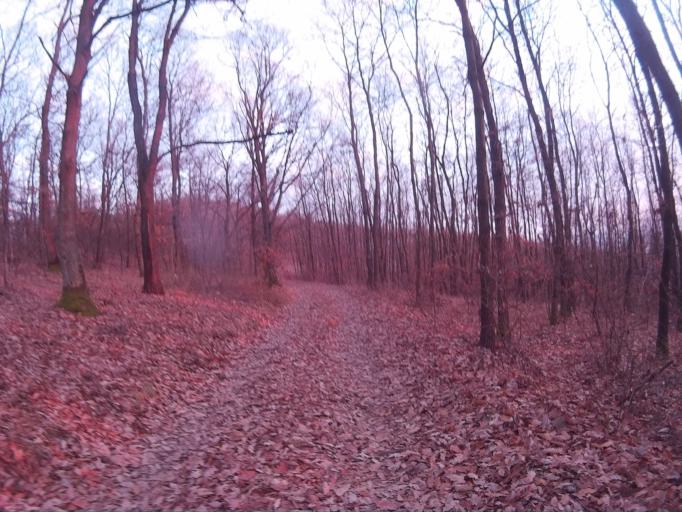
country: HU
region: Nograd
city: Rimoc
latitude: 48.0024
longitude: 19.4514
